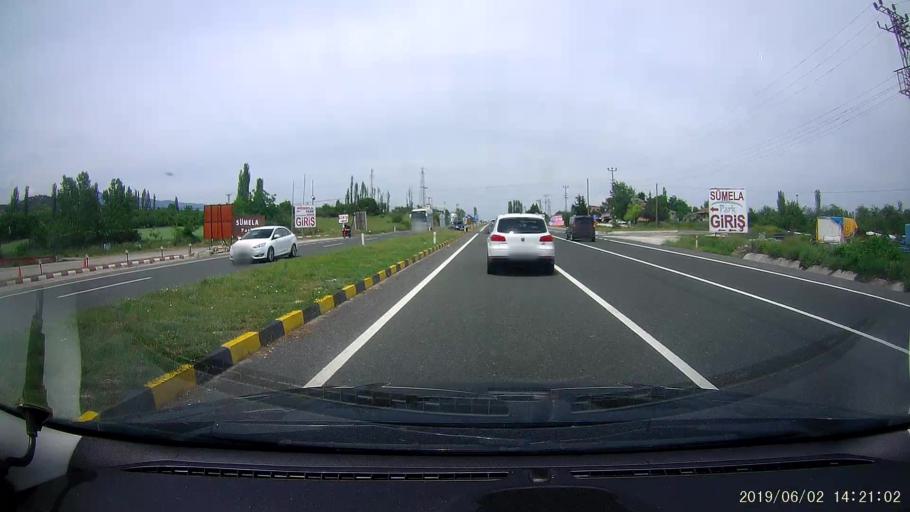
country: TR
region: Kastamonu
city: Tosya
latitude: 40.9752
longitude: 33.9989
